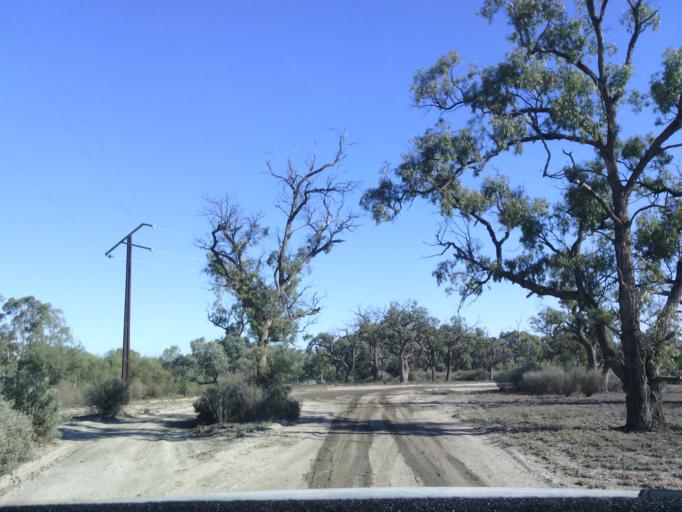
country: AU
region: South Australia
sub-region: Renmark Paringa
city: Renmark West
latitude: -34.2610
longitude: 140.6981
